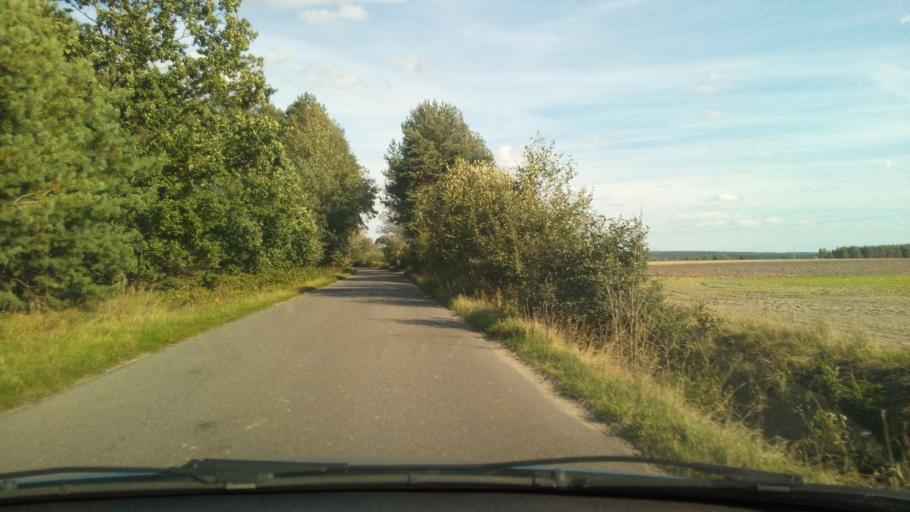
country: PL
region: Lodz Voivodeship
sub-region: Powiat piotrkowski
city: Sulejow
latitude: 51.4077
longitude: 19.8501
